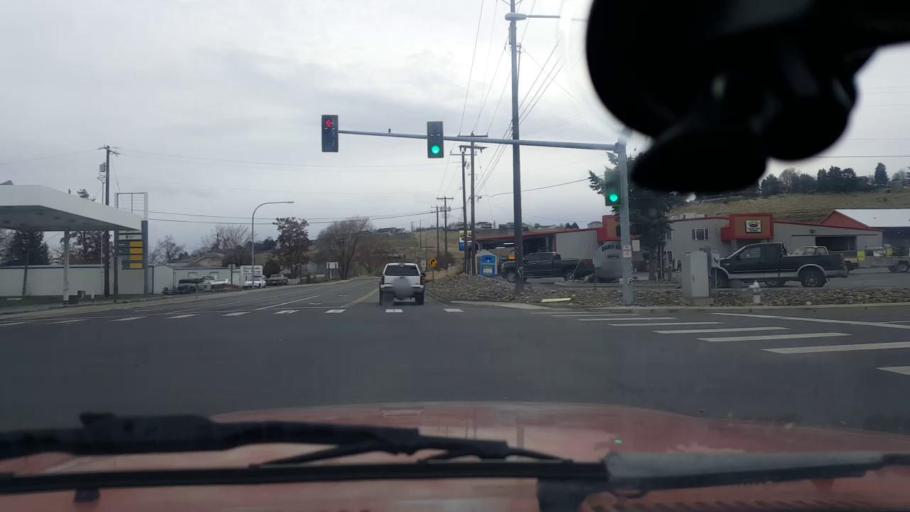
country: US
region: Washington
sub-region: Asotin County
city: West Clarkston-Highland
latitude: 46.4015
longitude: -117.0692
